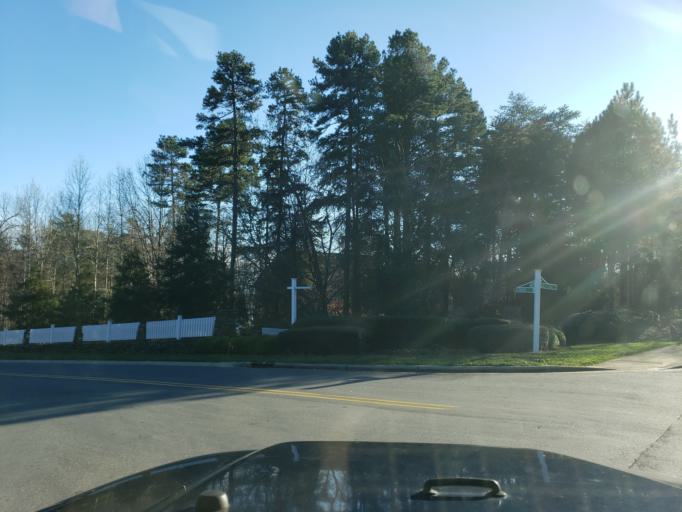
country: US
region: North Carolina
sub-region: Lincoln County
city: Westport
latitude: 35.5271
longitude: -80.9250
